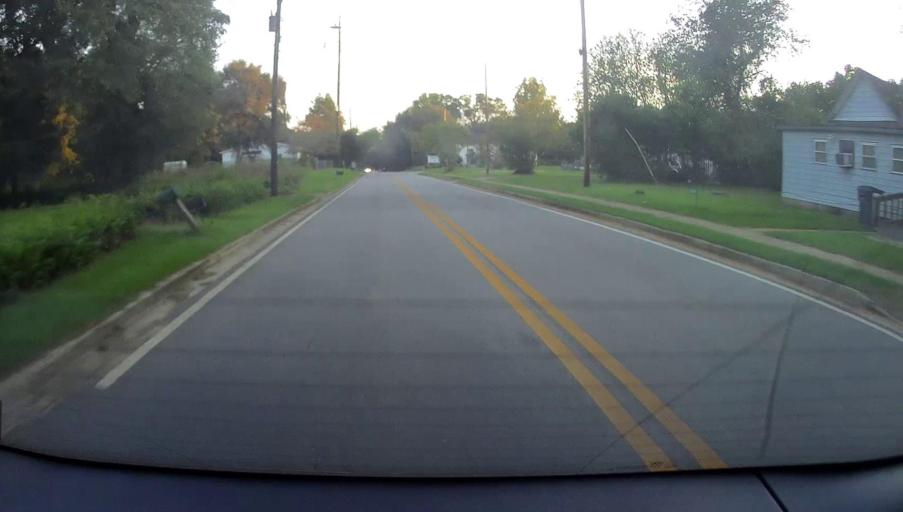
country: US
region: Georgia
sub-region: Houston County
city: Perry
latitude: 32.4627
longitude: -83.7386
